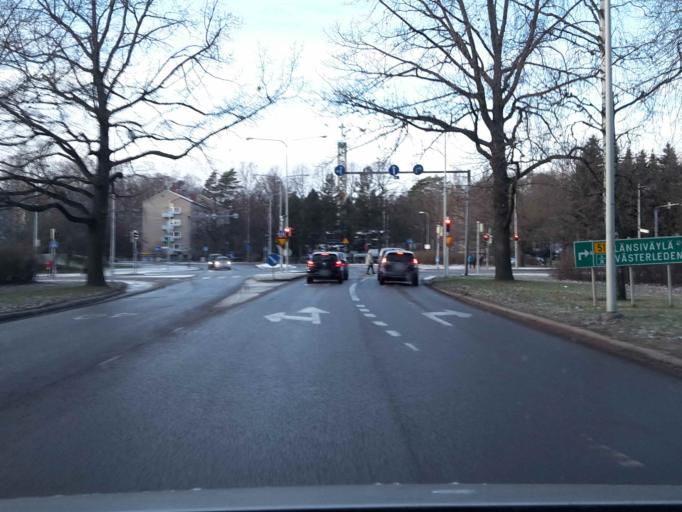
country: FI
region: Uusimaa
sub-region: Helsinki
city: Teekkarikylae
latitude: 60.1582
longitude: 24.8755
